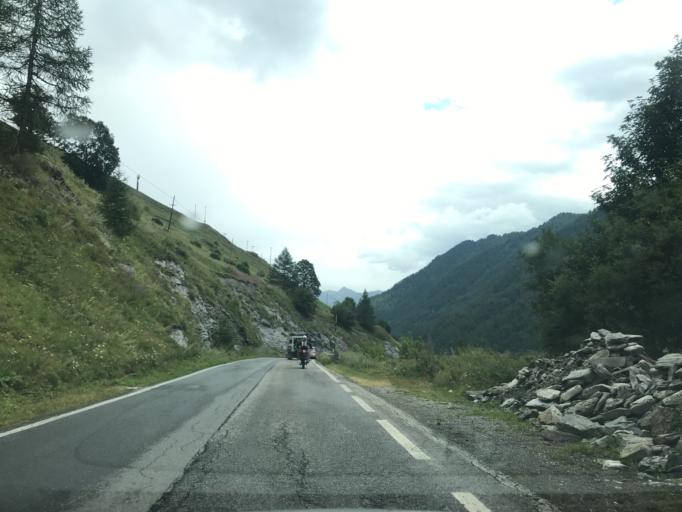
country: IT
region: Piedmont
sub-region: Provincia di Cuneo
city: Pontechianale
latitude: 44.6289
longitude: 7.0205
